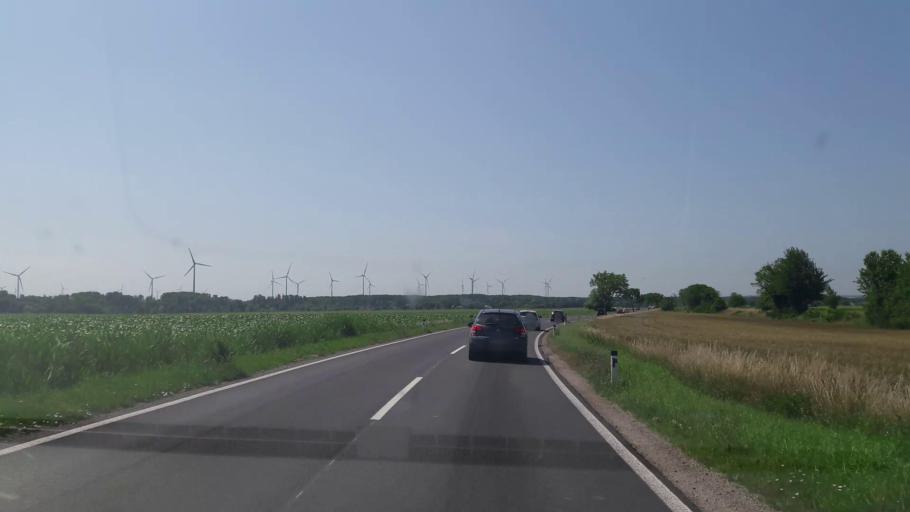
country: AT
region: Lower Austria
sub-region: Politischer Bezirk Bruck an der Leitha
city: Rohrau
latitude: 48.0816
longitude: 16.8632
